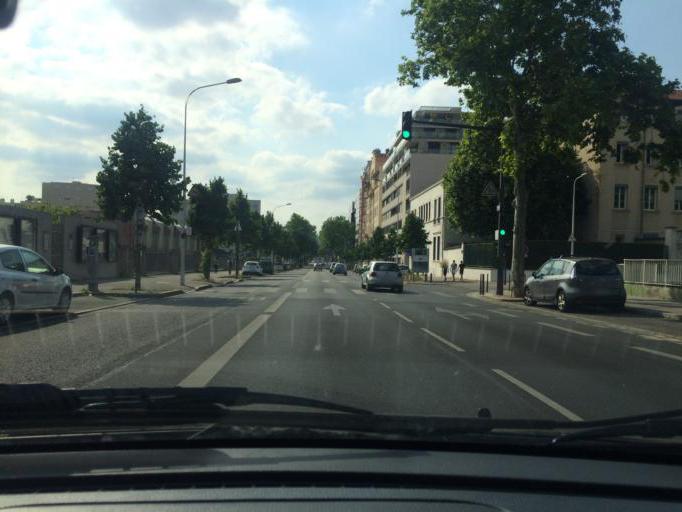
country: FR
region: Rhone-Alpes
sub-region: Departement du Rhone
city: Lyon
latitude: 45.7458
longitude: 4.8704
